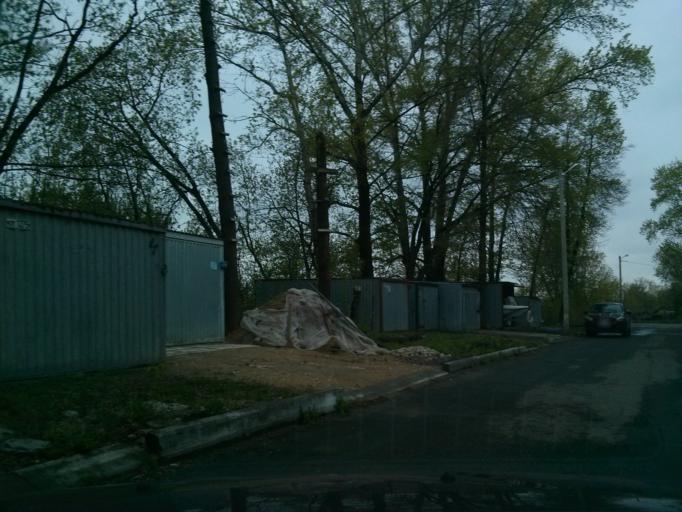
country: RU
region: Vladimir
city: Murom
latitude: 55.5668
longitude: 42.0731
